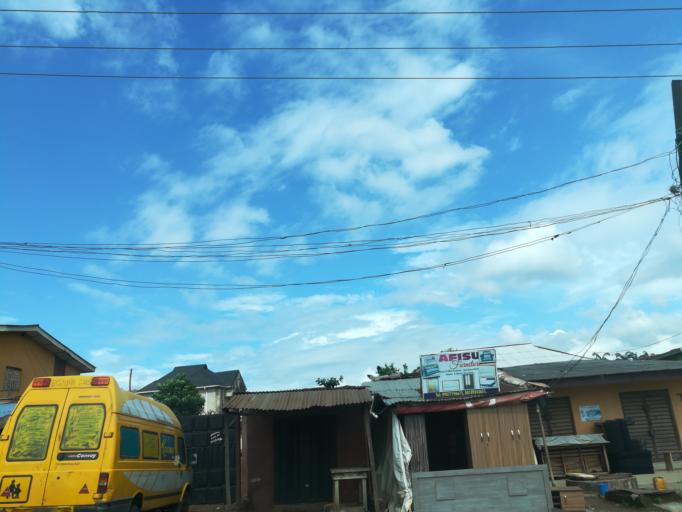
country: NG
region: Lagos
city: Ikorodu
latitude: 6.6016
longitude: 3.5183
